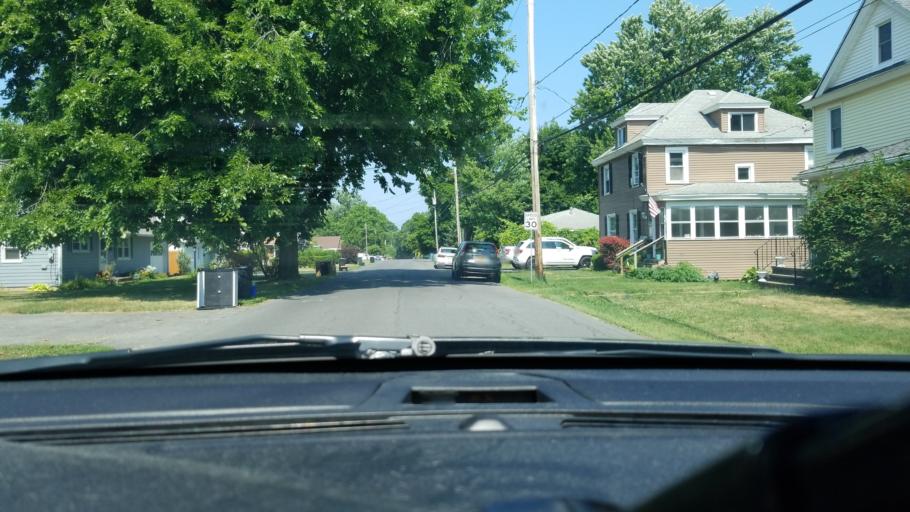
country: US
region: New York
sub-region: Onondaga County
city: Liverpool
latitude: 43.1132
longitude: -76.2148
